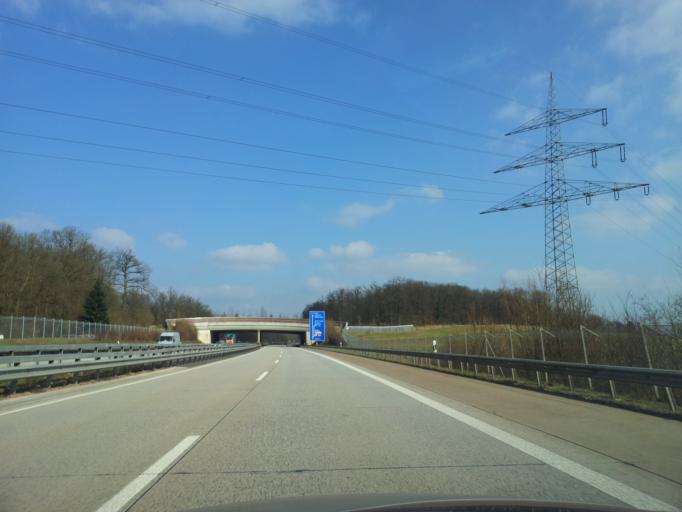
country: DE
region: Rheinland-Pfalz
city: Salmtal
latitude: 49.9326
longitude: 6.8737
